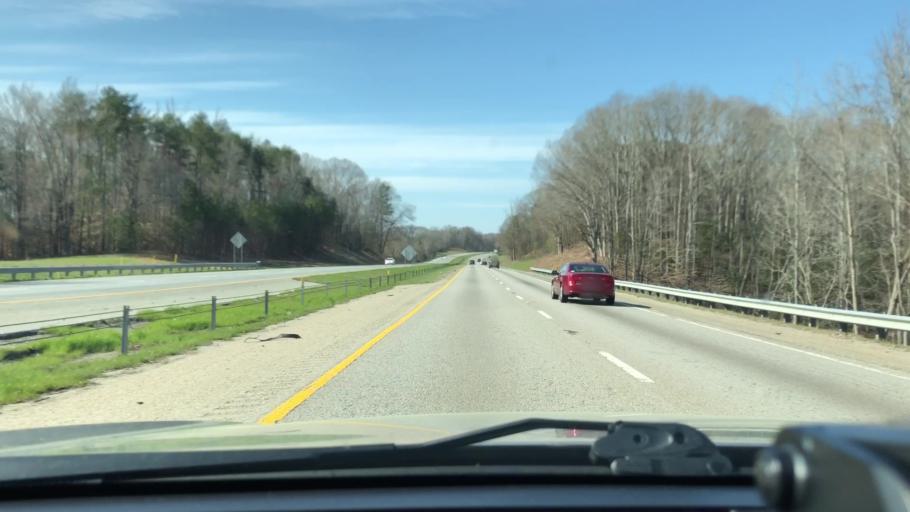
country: US
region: South Carolina
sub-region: Spartanburg County
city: Roebuck
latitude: 34.8617
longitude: -81.9824
